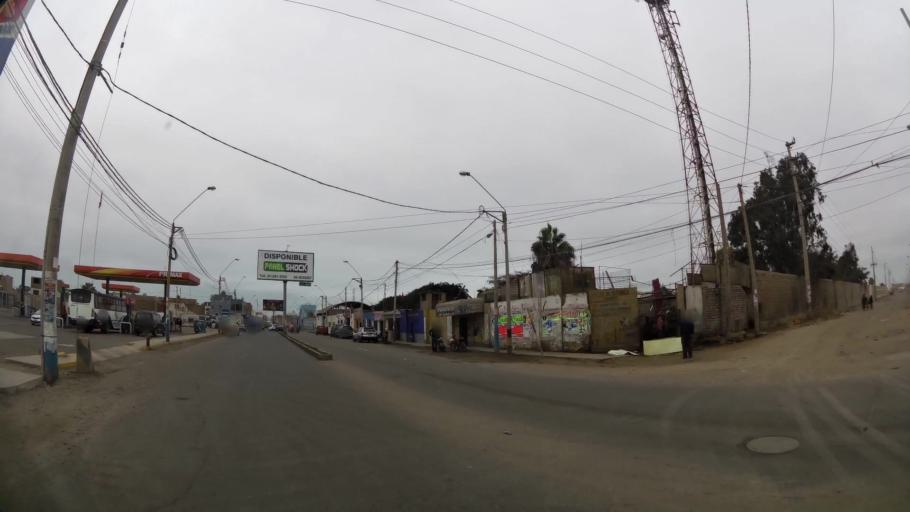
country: PE
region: Ica
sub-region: Provincia de Pisco
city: Pisco
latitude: -13.7109
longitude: -76.1967
